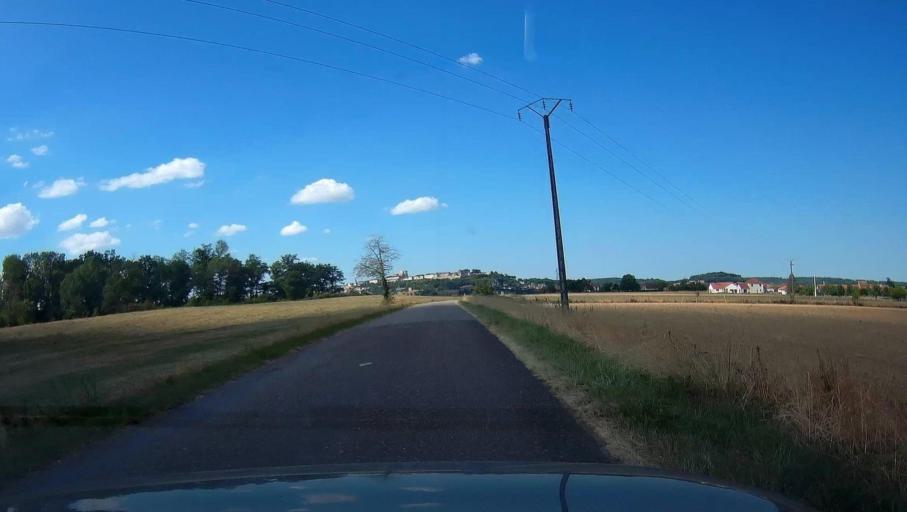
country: FR
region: Champagne-Ardenne
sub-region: Departement de la Haute-Marne
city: Langres
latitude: 47.8783
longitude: 5.3652
